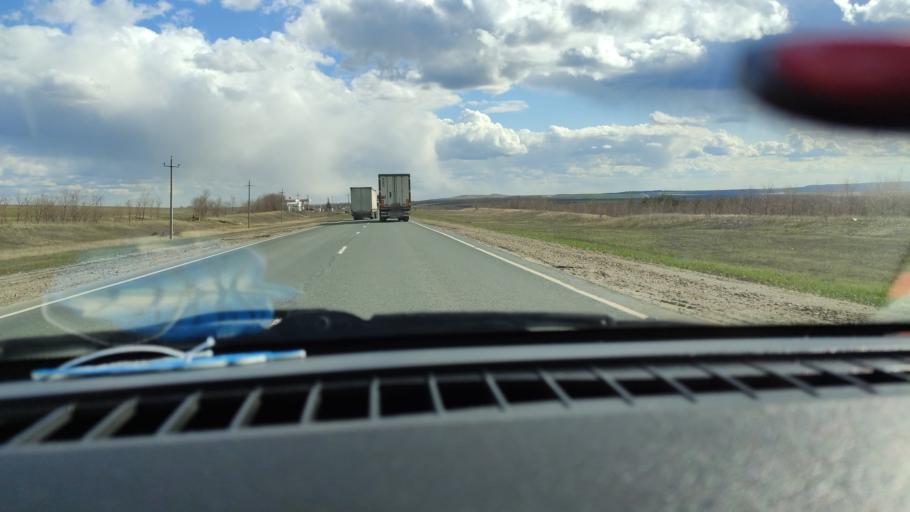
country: RU
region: Saratov
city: Alekseyevka
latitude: 52.2934
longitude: 47.9291
